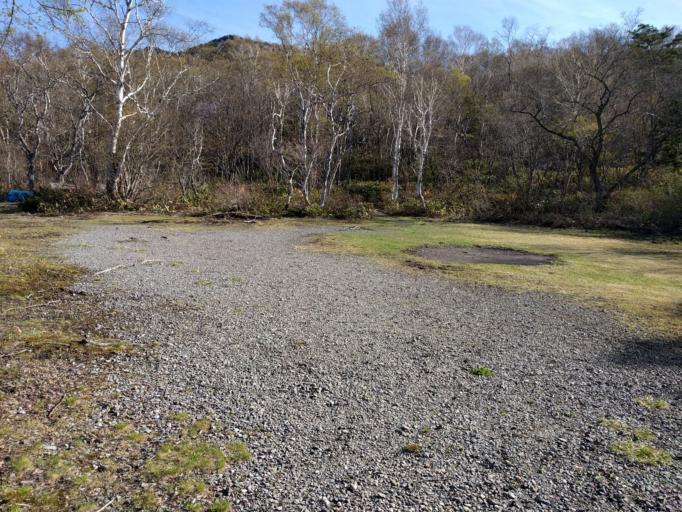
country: JP
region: Nagano
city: Nakano
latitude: 36.7192
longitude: 138.4813
